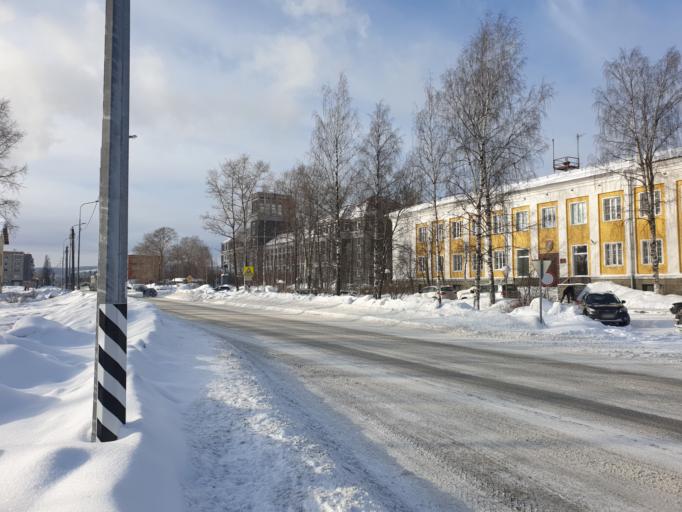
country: RU
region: Republic of Karelia
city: Medvezh'yegorsk
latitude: 62.9164
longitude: 34.4758
